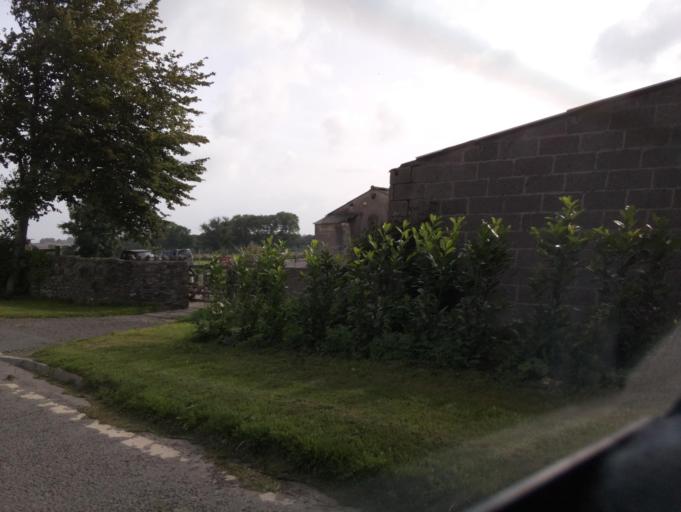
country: GB
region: England
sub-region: Somerset
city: Shepton Mallet
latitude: 51.2352
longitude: -2.5428
